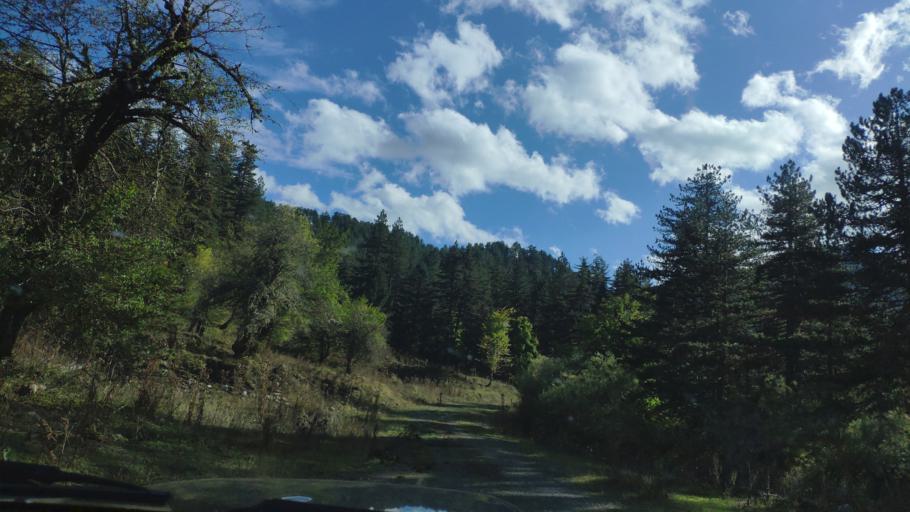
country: AL
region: Korce
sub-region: Rrethi i Devollit
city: Miras
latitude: 40.3973
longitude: 20.8817
